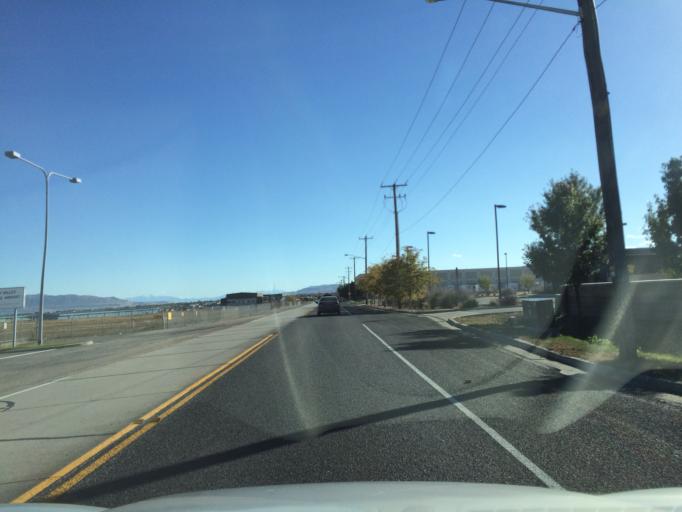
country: US
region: Utah
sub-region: Salt Lake County
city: Oquirrh
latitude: 40.6193
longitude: -111.9990
